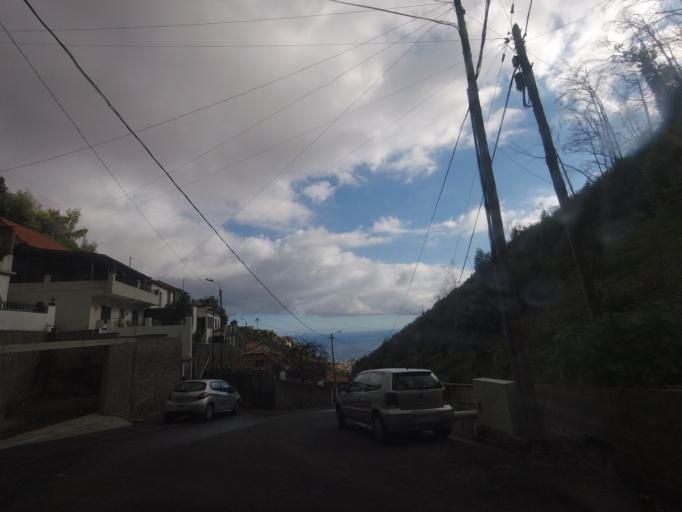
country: PT
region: Madeira
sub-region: Funchal
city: Nossa Senhora do Monte
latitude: 32.6772
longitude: -16.9317
